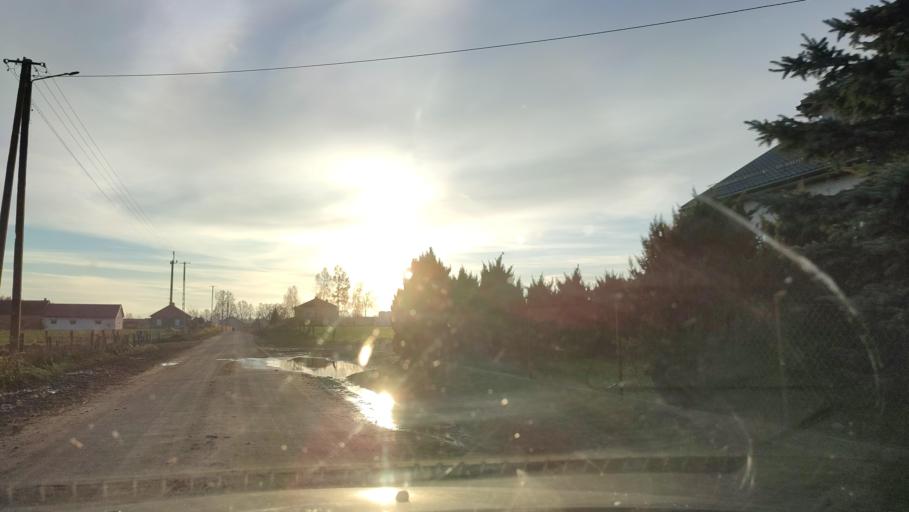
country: PL
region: Masovian Voivodeship
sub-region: Powiat mlawski
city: Dzierzgowo
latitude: 53.2823
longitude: 20.6519
